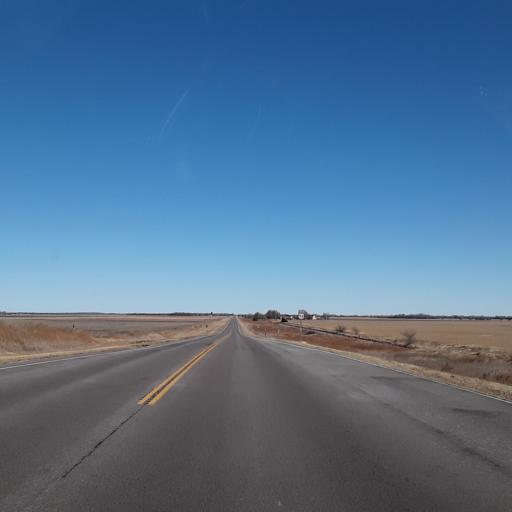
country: US
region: Kansas
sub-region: Pawnee County
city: Larned
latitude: 38.0893
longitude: -99.2234
